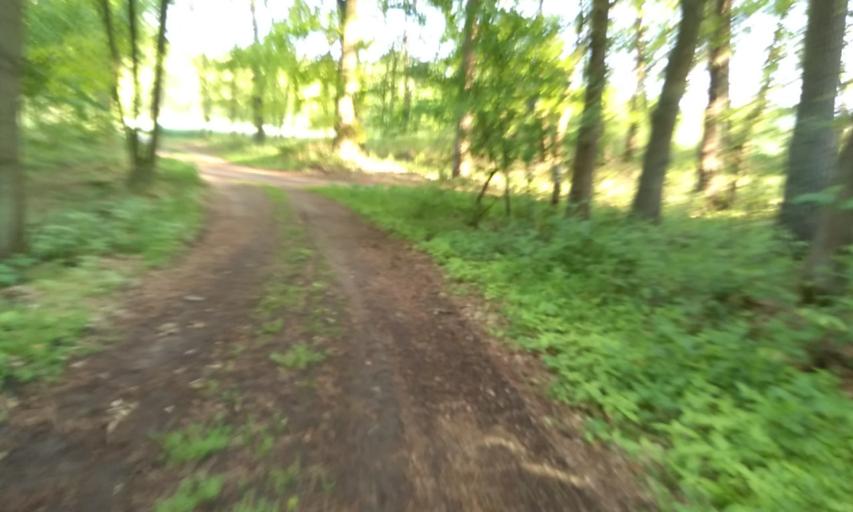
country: DE
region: Lower Saxony
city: Bliedersdorf
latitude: 53.4909
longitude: 9.5424
